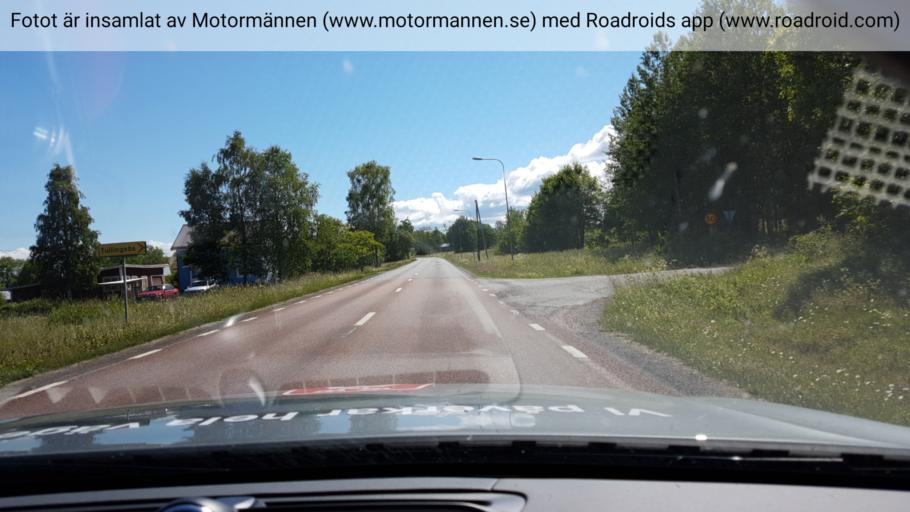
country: SE
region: Jaemtland
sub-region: Stroemsunds Kommun
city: Stroemsund
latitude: 63.8245
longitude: 15.5145
